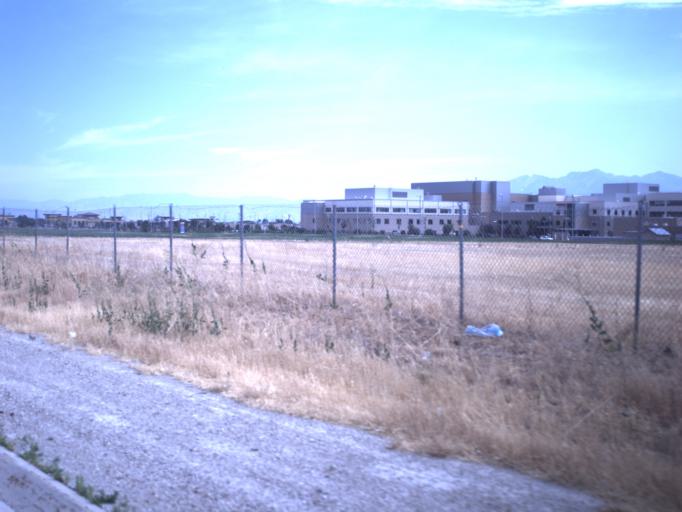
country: US
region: Utah
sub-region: Salt Lake County
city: Riverton
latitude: 40.5180
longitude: -111.9840
